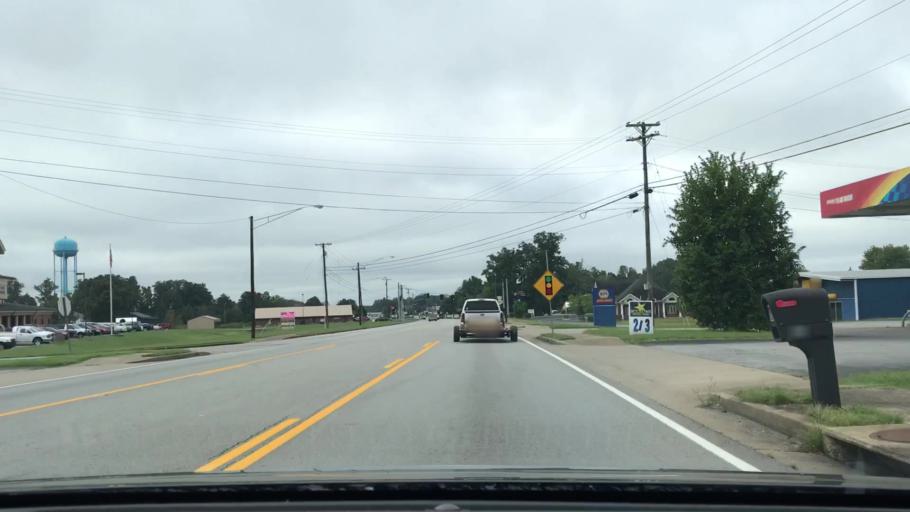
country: US
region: Kentucky
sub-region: Russell County
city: Russell Springs
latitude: 37.0359
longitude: -85.0755
